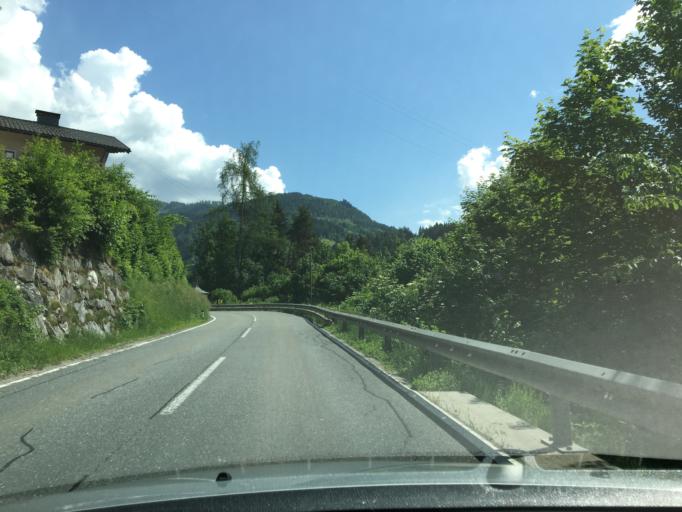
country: AT
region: Salzburg
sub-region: Politischer Bezirk Sankt Johann im Pongau
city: Sankt Johann im Pongau
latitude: 47.3442
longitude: 13.2078
